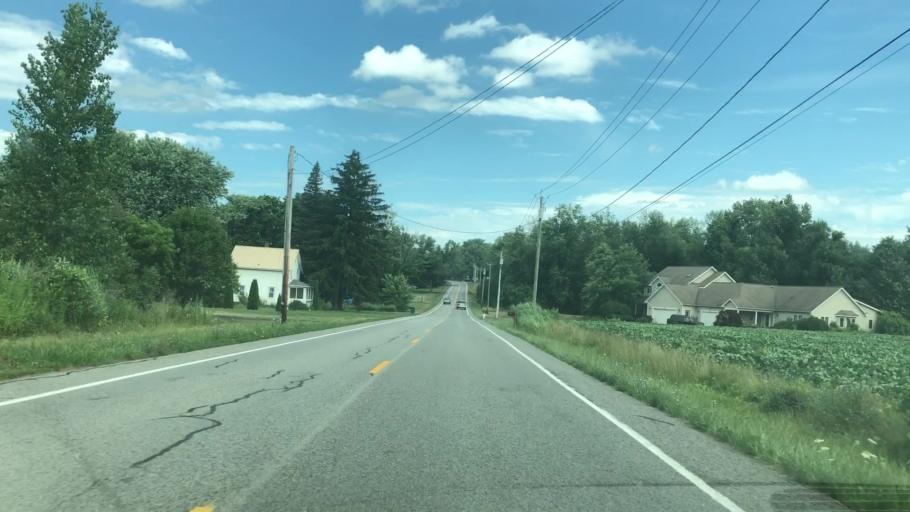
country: US
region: New York
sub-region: Wayne County
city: Macedon
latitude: 43.1191
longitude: -77.3526
